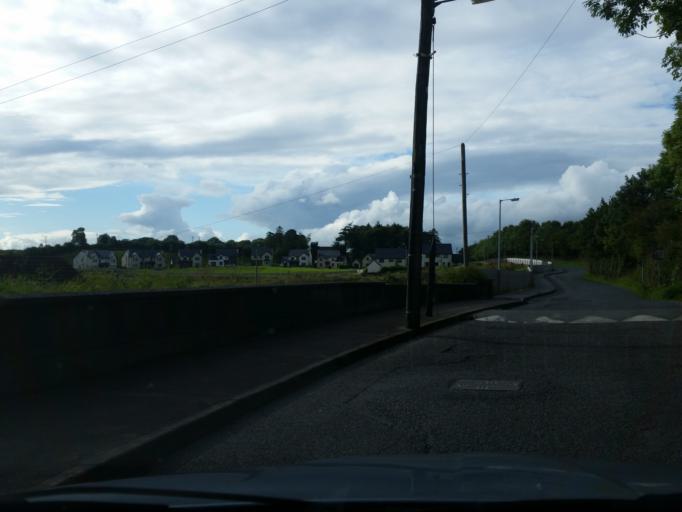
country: IE
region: Ulster
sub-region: County Monaghan
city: Clones
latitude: 54.1886
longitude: -7.2379
